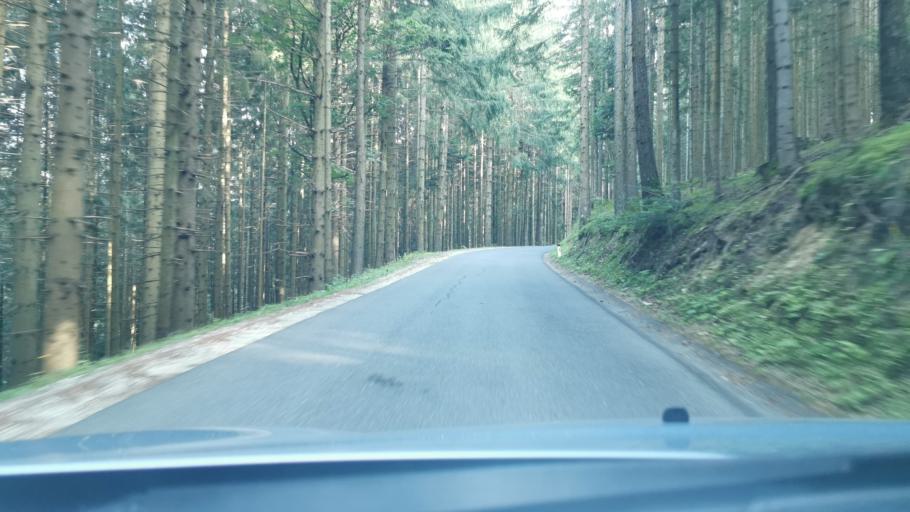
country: AT
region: Styria
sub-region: Politischer Bezirk Weiz
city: Fischbach
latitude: 47.3905
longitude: 15.6418
